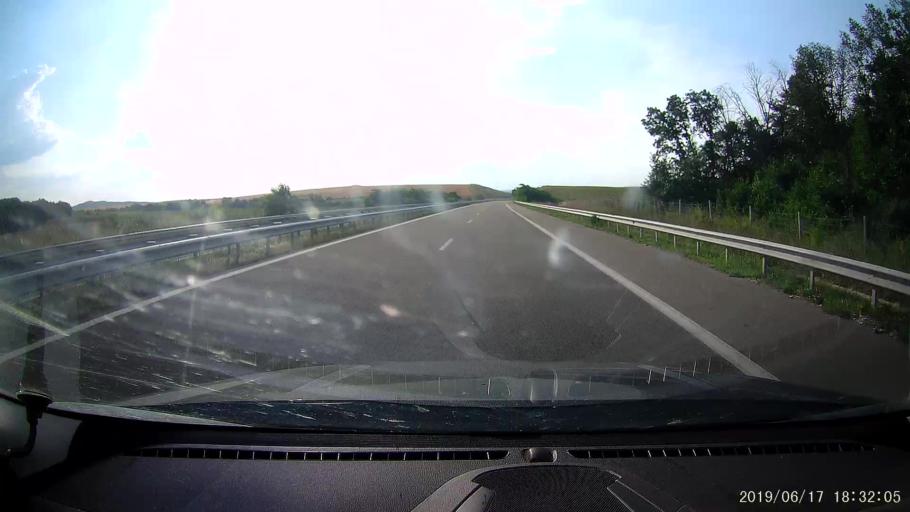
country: BG
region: Khaskovo
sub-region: Obshtina Dimitrovgrad
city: Dimitrovgrad
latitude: 42.0546
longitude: 25.4877
